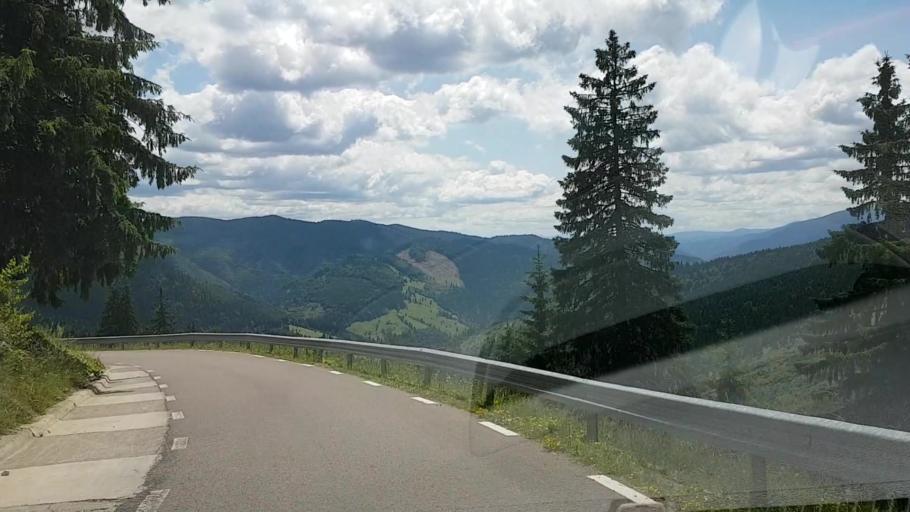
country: RO
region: Suceava
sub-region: Municipiul Campulung Moldovenesc
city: Campulung Moldovenesc
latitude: 47.4371
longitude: 25.5593
